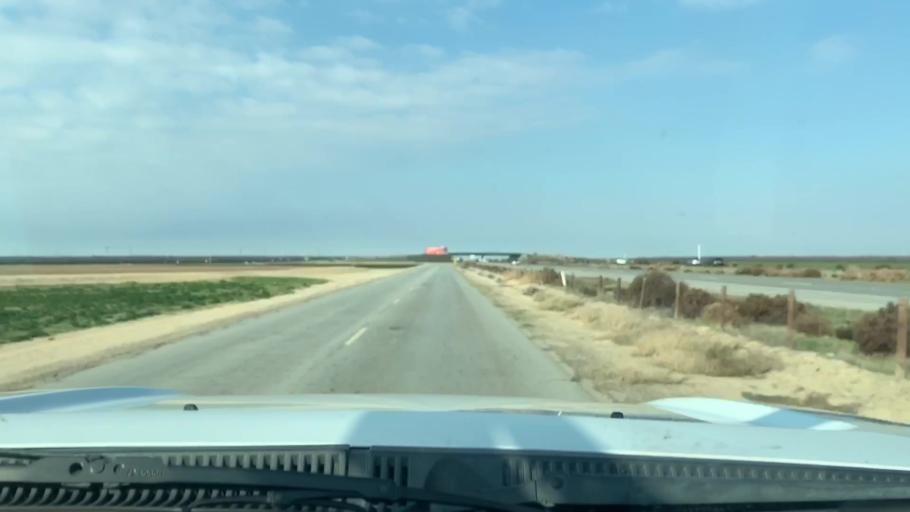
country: US
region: California
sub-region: Kern County
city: Buttonwillow
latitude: 35.4509
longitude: -119.4692
